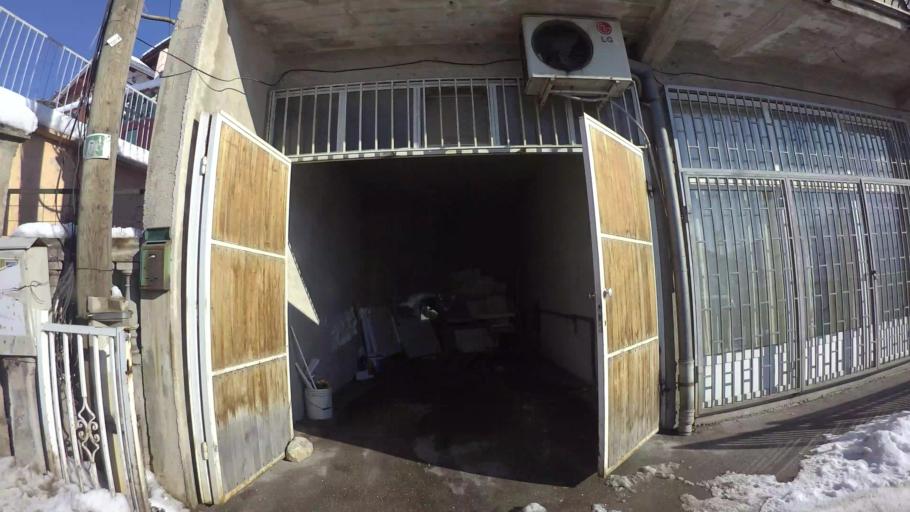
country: BA
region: Federation of Bosnia and Herzegovina
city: Kobilja Glava
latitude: 43.8741
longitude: 18.4233
